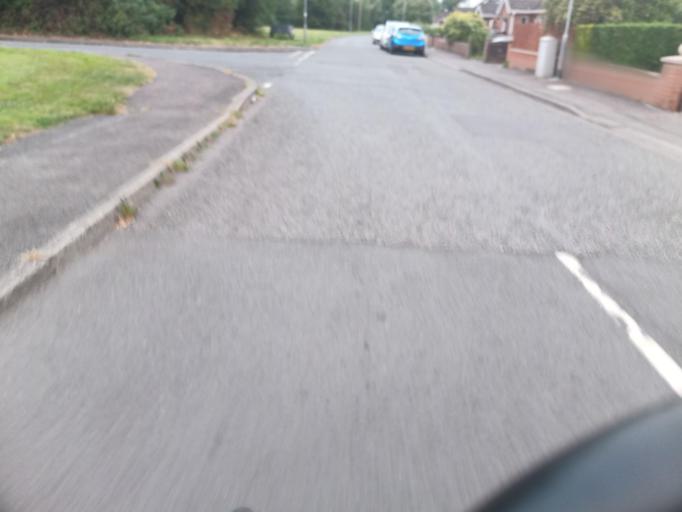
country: GB
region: Northern Ireland
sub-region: Ards District
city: Comber
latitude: 54.5525
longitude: -5.7295
